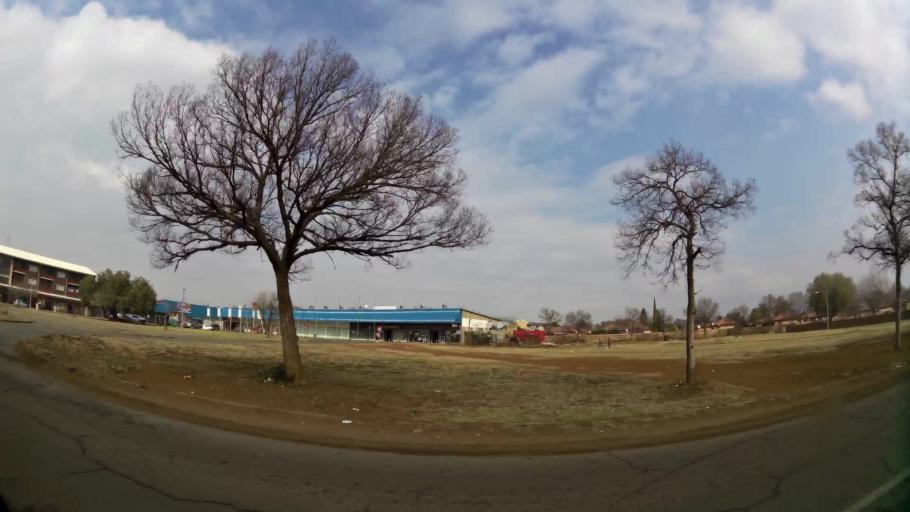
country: ZA
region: Gauteng
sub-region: Sedibeng District Municipality
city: Vanderbijlpark
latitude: -26.6908
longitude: 27.8417
